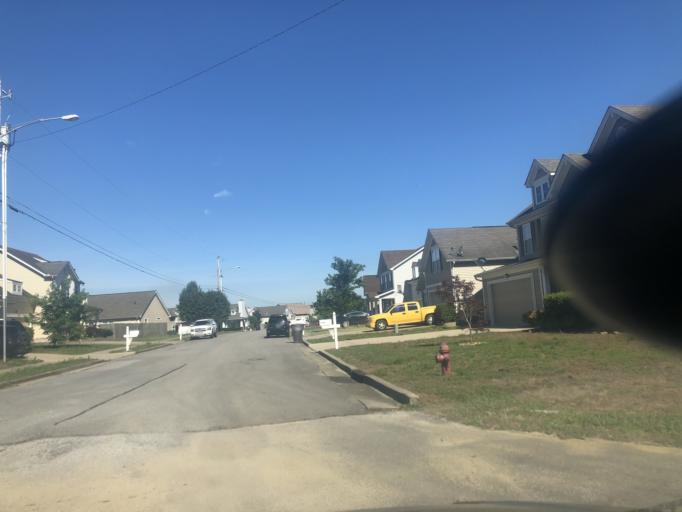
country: US
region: Tennessee
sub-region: Davidson County
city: Lakewood
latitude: 36.2426
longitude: -86.6622
